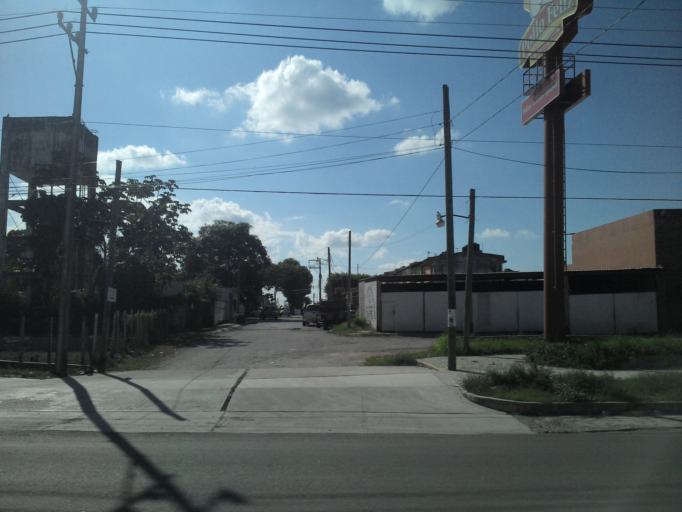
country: MX
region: Chiapas
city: Palenque
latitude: 17.5192
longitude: -91.9936
